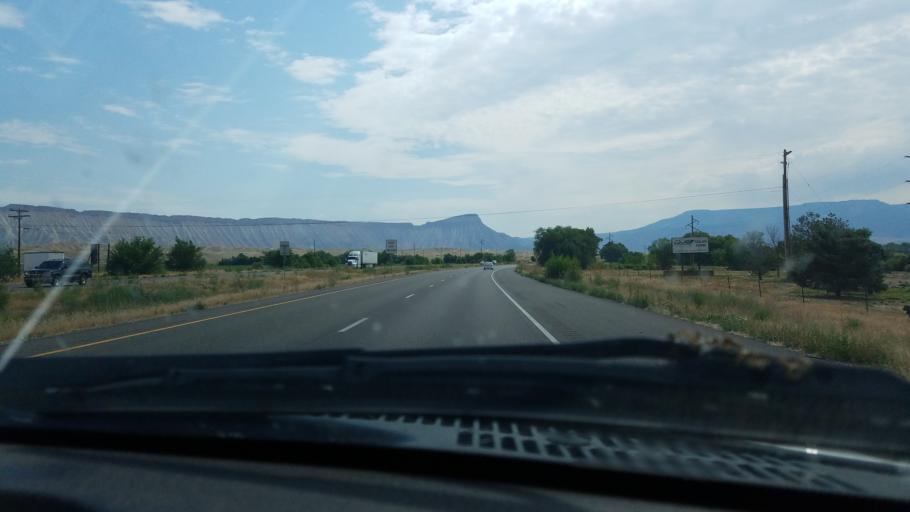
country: US
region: Colorado
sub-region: Mesa County
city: Fruitvale
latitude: 39.1081
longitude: -108.5105
